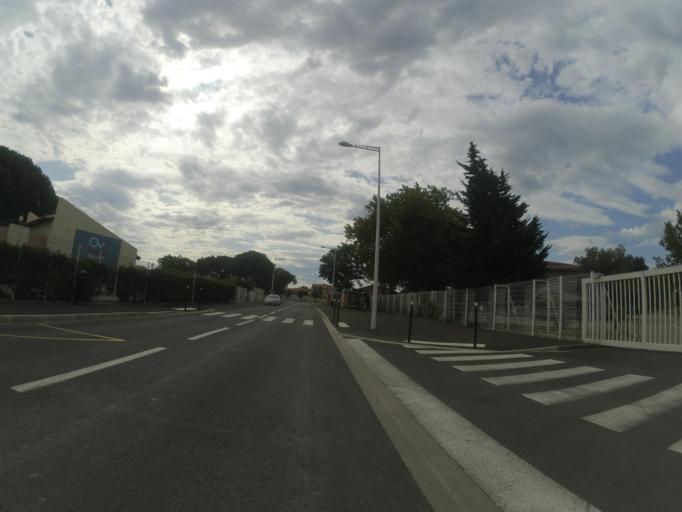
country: FR
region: Languedoc-Roussillon
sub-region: Departement des Pyrenees-Orientales
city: Toulouges
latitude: 42.6752
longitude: 2.8488
